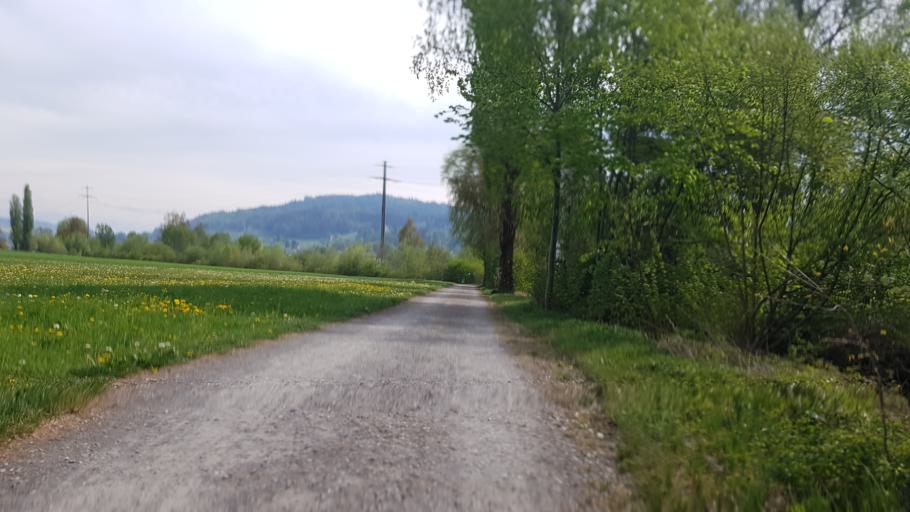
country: CH
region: Aargau
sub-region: Bezirk Kulm
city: Gontenschwil
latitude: 47.2802
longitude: 8.1510
